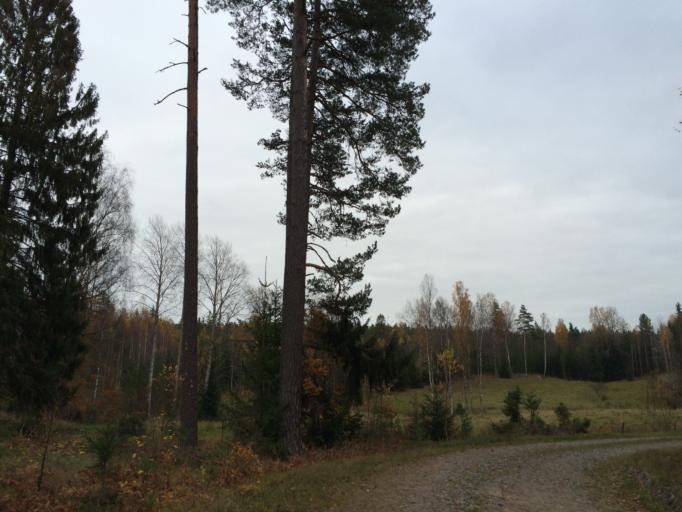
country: SE
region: OEstergoetland
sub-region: Linkopings Kommun
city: Ljungsbro
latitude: 58.7275
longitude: 15.5185
